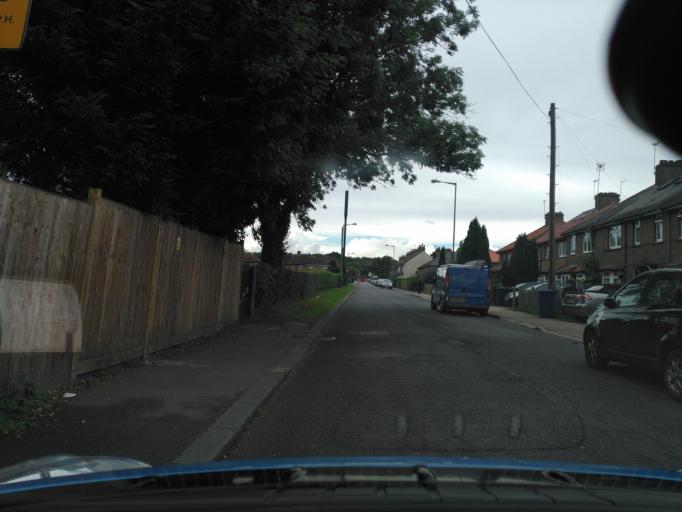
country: GB
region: England
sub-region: Greater London
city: High Barnet
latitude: 51.6442
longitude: -0.2117
